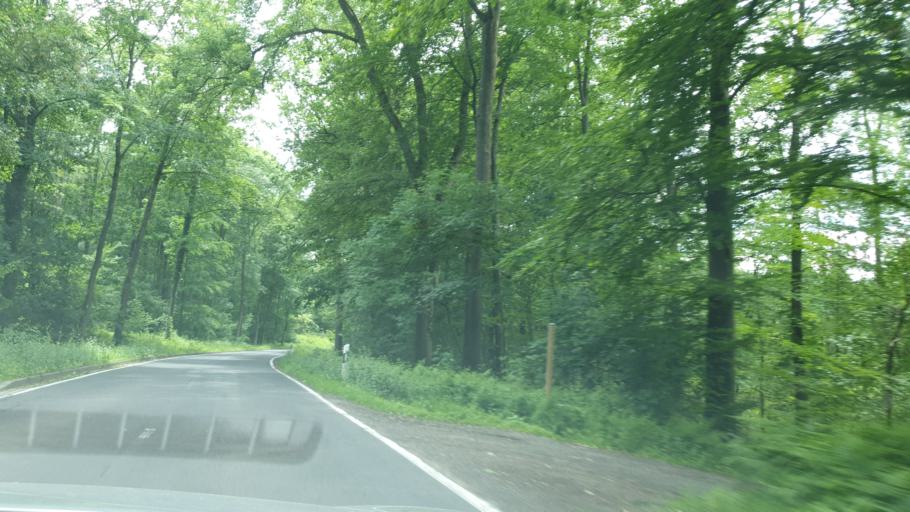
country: DE
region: Rheinland-Pfalz
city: Neuhausel
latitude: 50.3936
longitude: 7.7148
